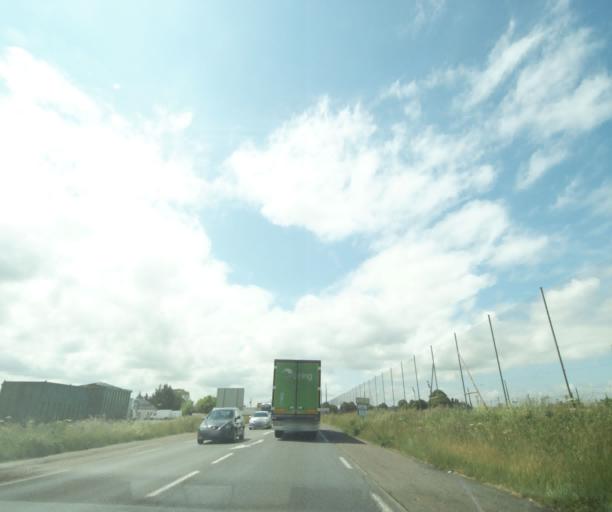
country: FR
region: Poitou-Charentes
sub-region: Departement des Deux-Sevres
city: Thouars
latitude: 46.9881
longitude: -0.1972
